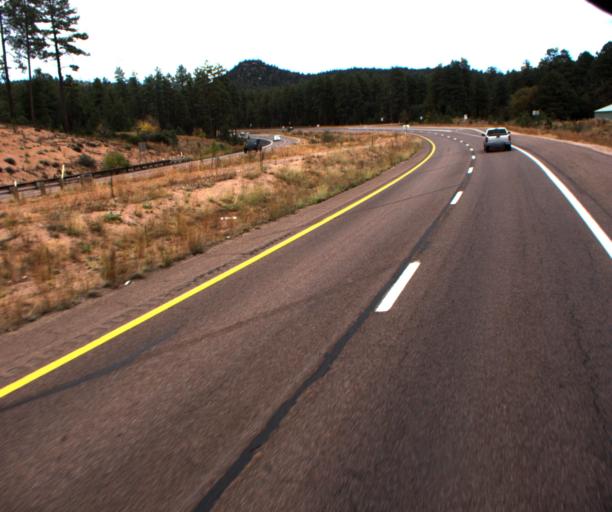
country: US
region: Arizona
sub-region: Gila County
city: Star Valley
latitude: 34.2819
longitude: -111.1457
